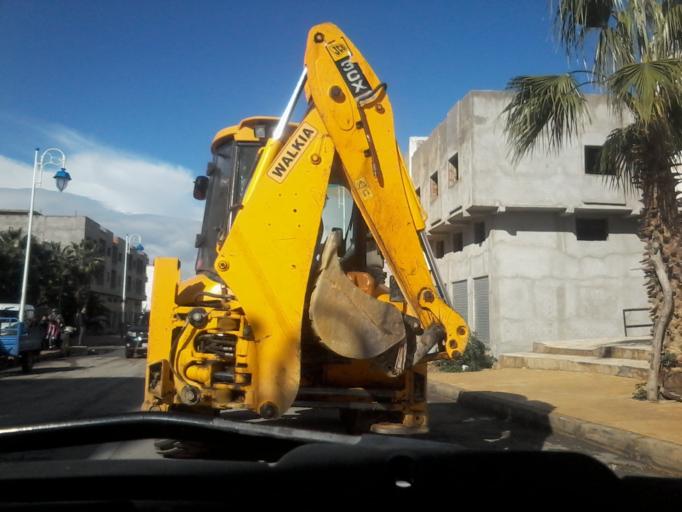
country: MA
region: Tanger-Tetouan
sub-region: Tetouan
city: Martil
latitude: 35.6993
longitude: -5.3483
